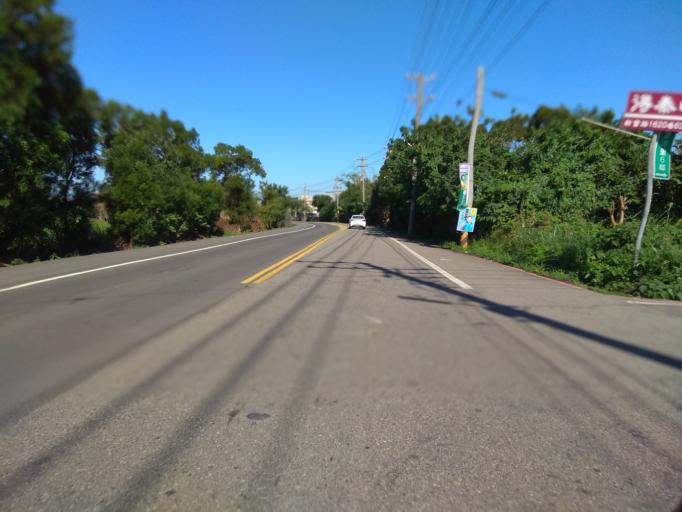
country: TW
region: Taiwan
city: Taoyuan City
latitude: 24.9865
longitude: 121.1346
